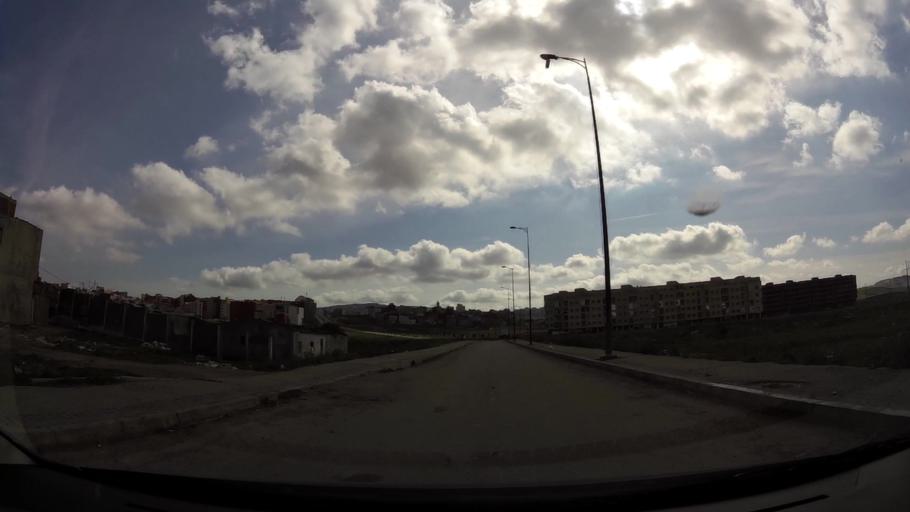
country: MA
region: Tanger-Tetouan
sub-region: Tanger-Assilah
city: Tangier
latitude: 35.7642
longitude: -5.7722
